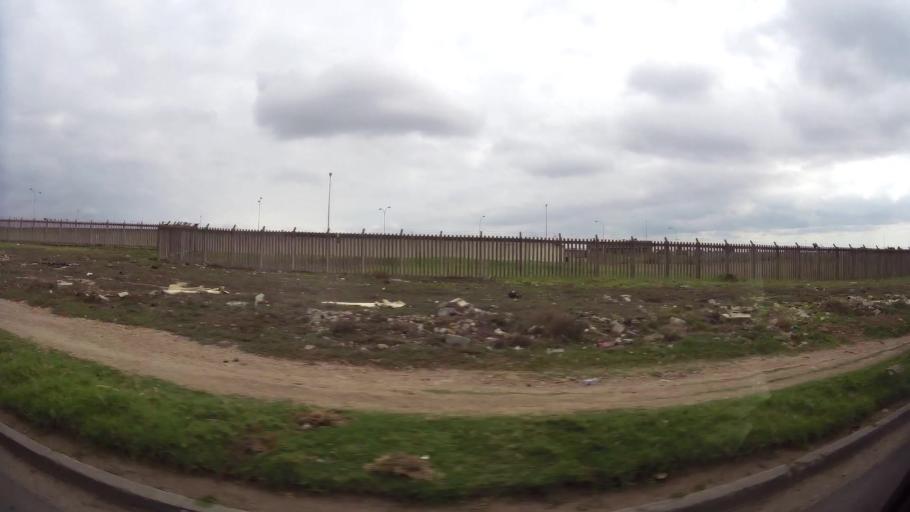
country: ZA
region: Eastern Cape
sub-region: Nelson Mandela Bay Metropolitan Municipality
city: Port Elizabeth
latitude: -33.8752
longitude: 25.5623
